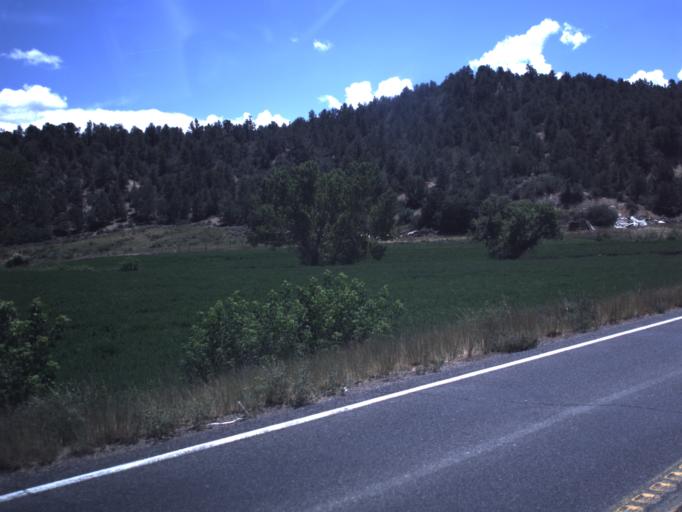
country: US
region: Utah
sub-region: Kane County
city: Kanab
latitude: 37.3298
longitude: -112.5998
